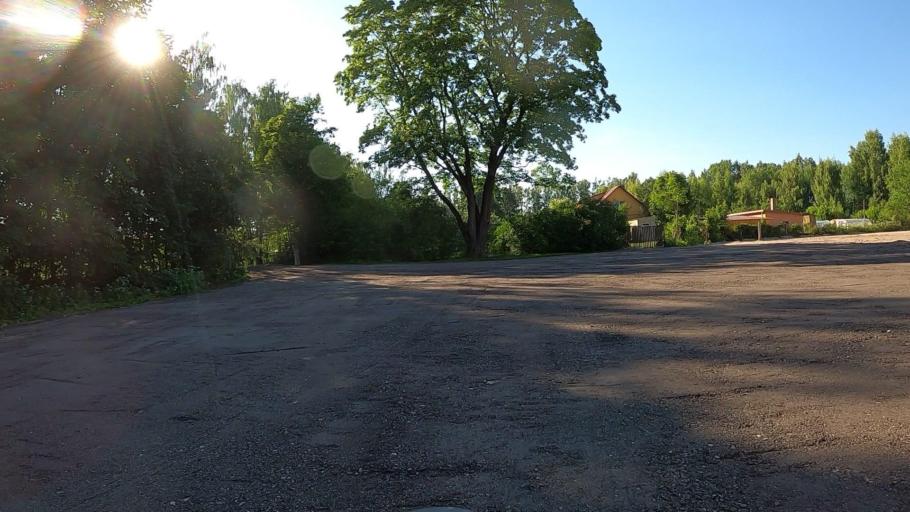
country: LV
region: Kekava
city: Kekava
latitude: 56.8819
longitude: 24.2604
